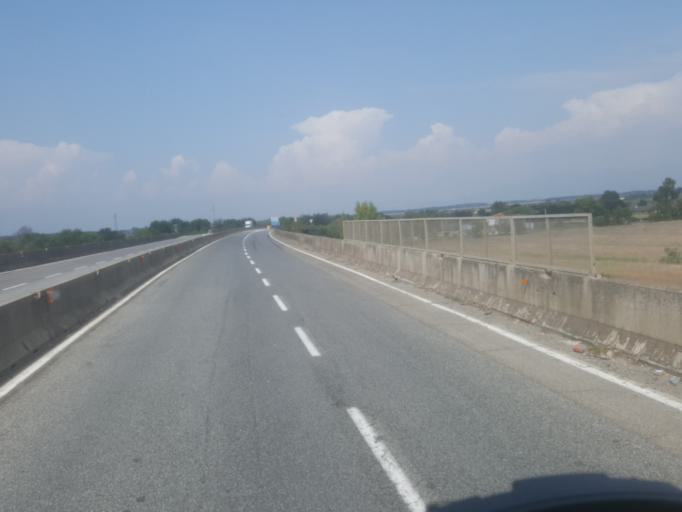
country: IT
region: Tuscany
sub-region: Provincia di Livorno
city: Guasticce
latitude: 43.5944
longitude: 10.3588
